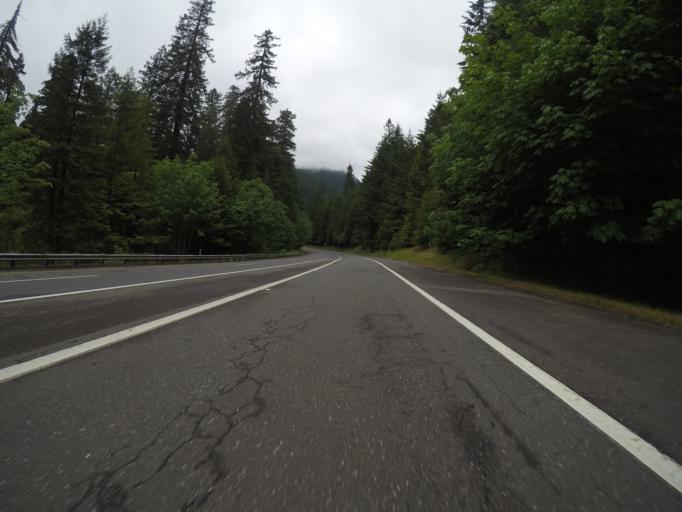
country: US
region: California
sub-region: Humboldt County
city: Rio Dell
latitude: 40.4441
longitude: -124.0397
